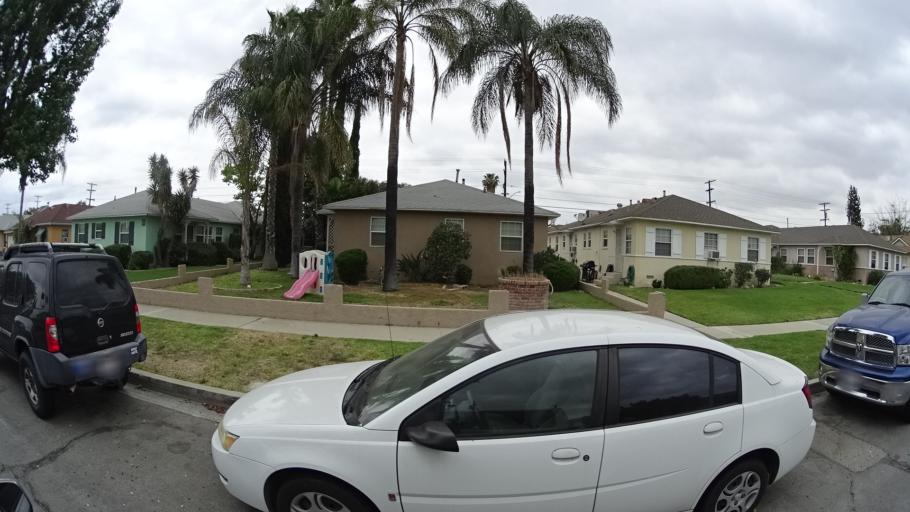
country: US
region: California
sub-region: Los Angeles County
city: Burbank
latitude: 34.2017
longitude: -118.3357
